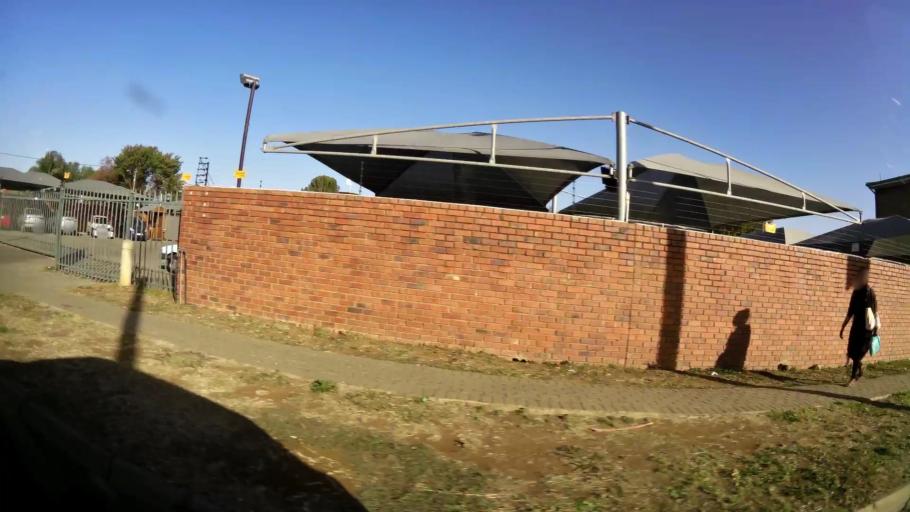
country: ZA
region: Gauteng
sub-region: City of Tshwane Metropolitan Municipality
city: Pretoria
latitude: -25.7177
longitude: 28.2094
